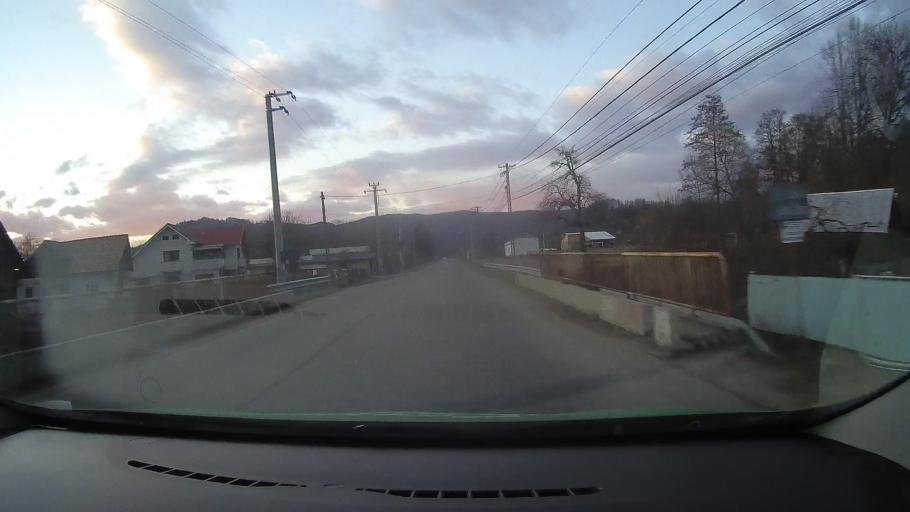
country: RO
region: Dambovita
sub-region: Comuna Valea Lunga
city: Valea Lunga-Cricov
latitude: 45.0658
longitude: 25.5849
